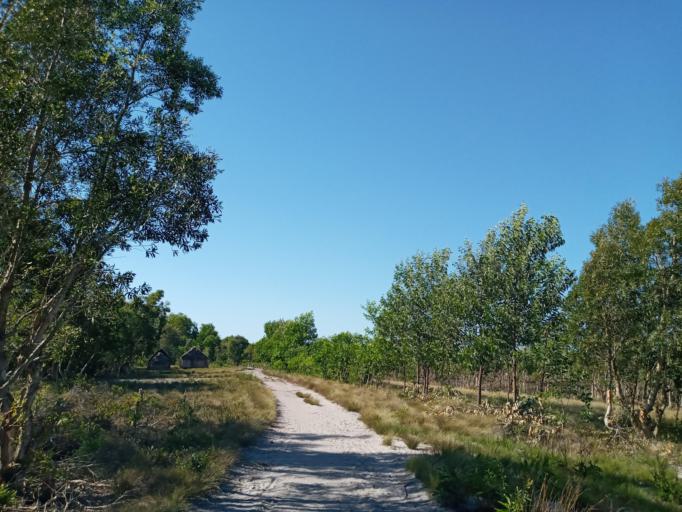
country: MG
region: Anosy
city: Fort Dauphin
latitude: -24.9069
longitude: 47.0964
